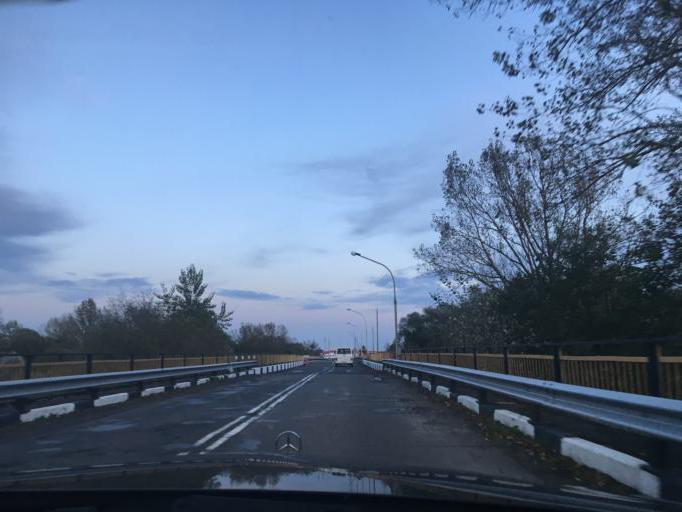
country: PL
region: Lublin Voivodeship
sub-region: Powiat bialski
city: Slawatycze
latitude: 51.7659
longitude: 23.5917
